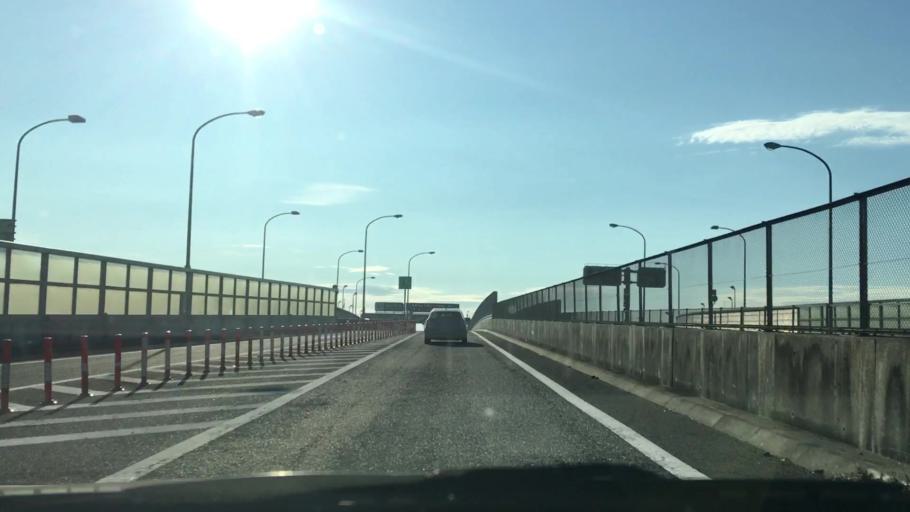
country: JP
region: Tokyo
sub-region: Machida-shi
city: Machida
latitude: 35.5479
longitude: 139.5367
